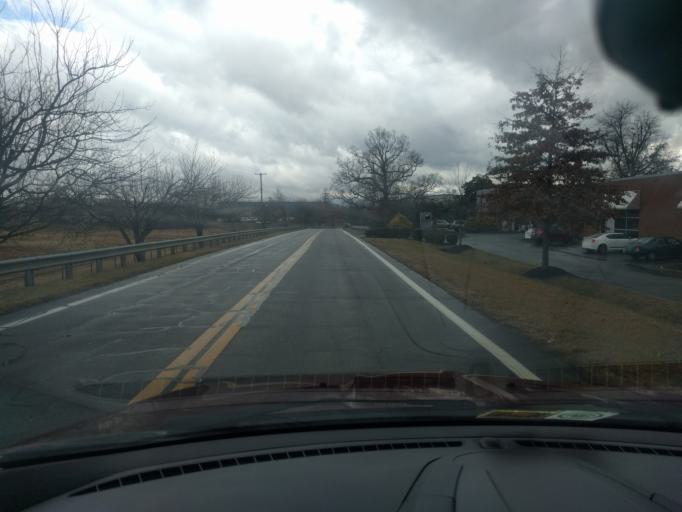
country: US
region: Virginia
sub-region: Roanoke County
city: Hollins
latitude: 37.3166
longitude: -79.9792
